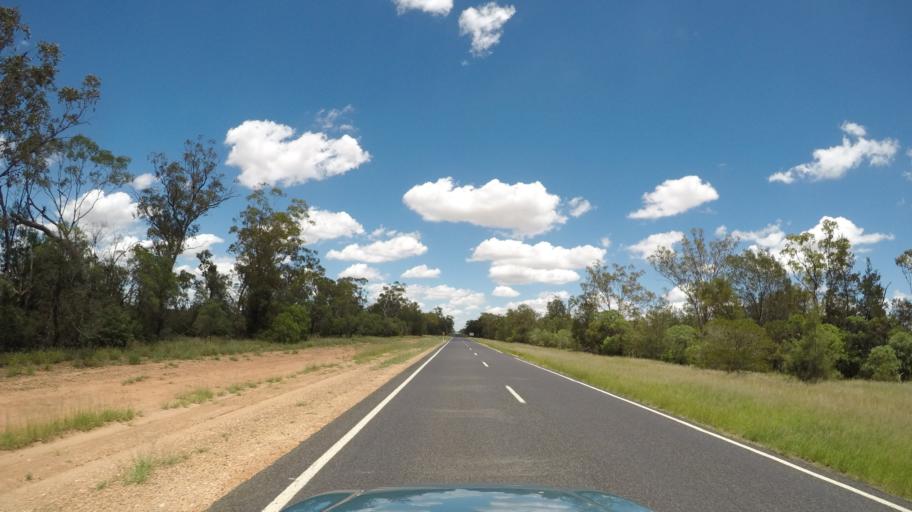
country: AU
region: Queensland
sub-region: Goondiwindi
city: Goondiwindi
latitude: -28.1647
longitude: 150.6101
